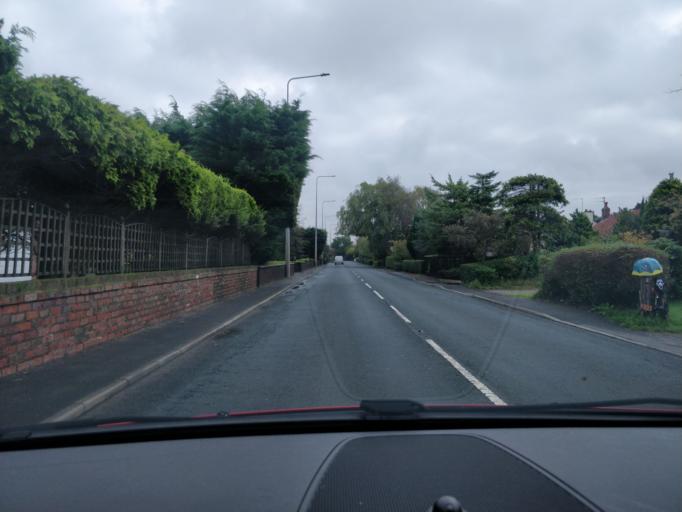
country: GB
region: England
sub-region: Sefton
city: Southport
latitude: 53.6197
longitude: -2.9519
